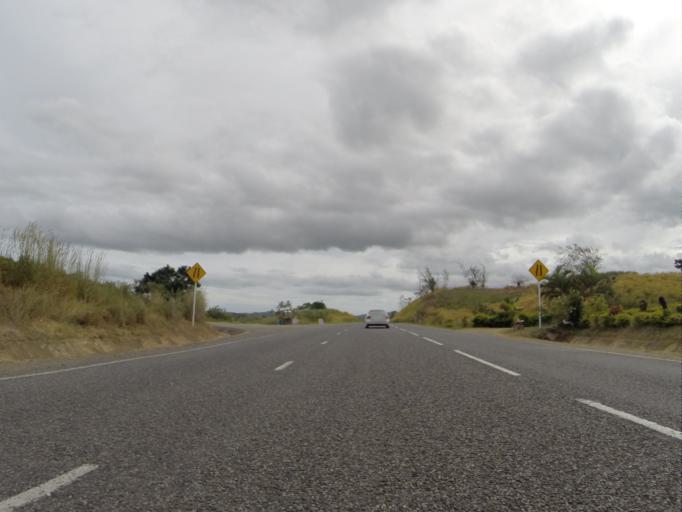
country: FJ
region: Western
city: Nadi
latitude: -18.0324
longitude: 177.3330
